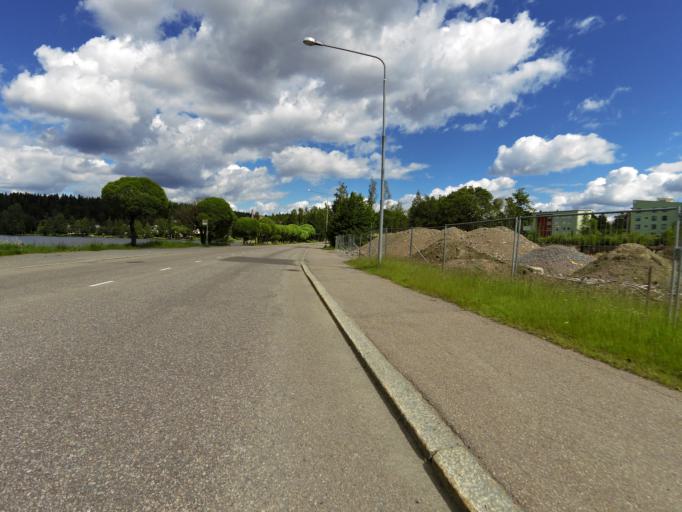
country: FI
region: Pirkanmaa
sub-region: Tampere
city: Pirkkala
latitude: 61.5068
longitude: 23.6571
